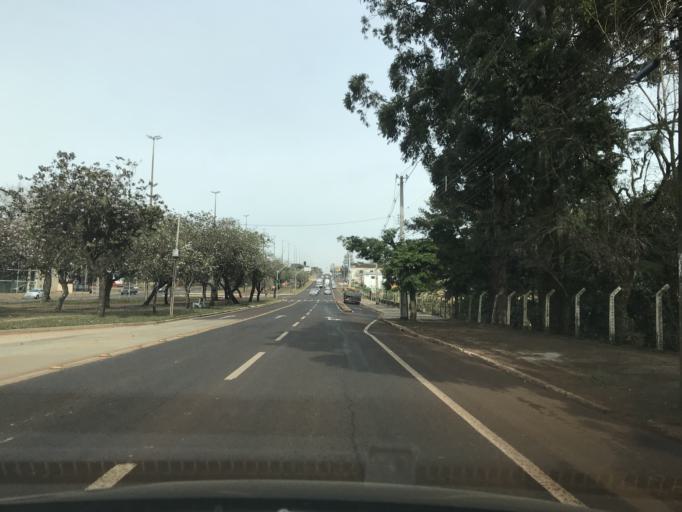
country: BR
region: Parana
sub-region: Cascavel
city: Cascavel
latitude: -24.9722
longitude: -53.4907
